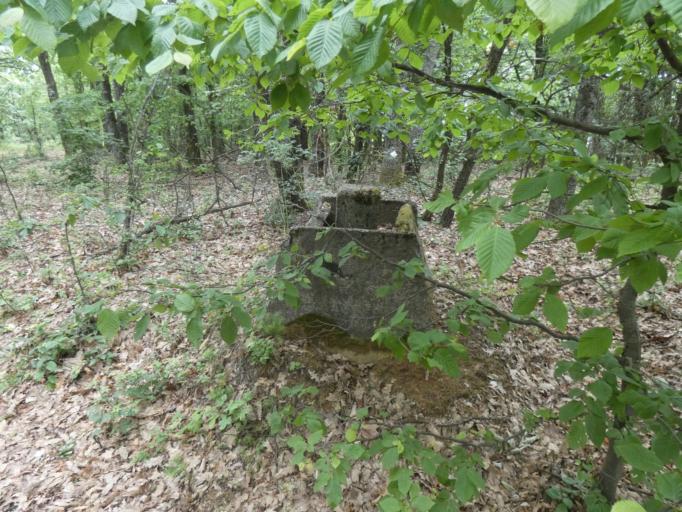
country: HU
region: Heves
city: Petervasara
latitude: 48.1091
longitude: 20.0723
